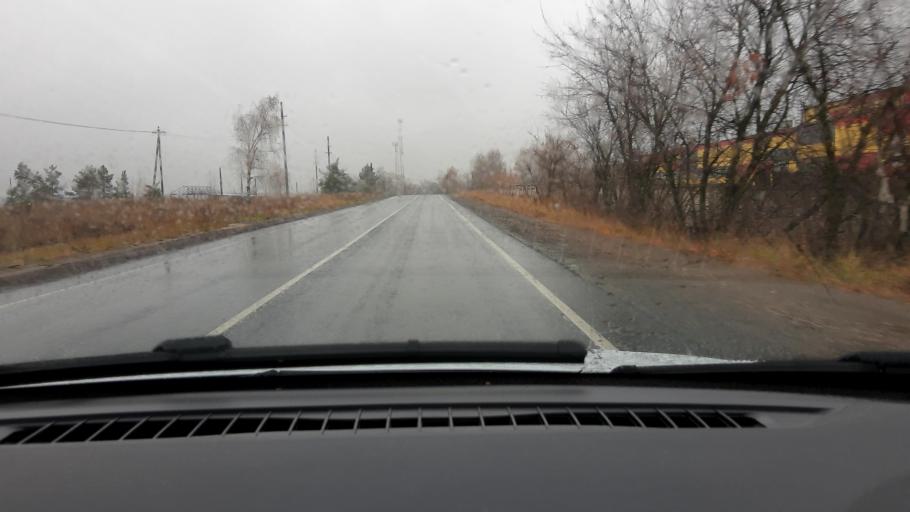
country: RU
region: Nizjnij Novgorod
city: Babino
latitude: 56.2859
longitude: 43.5996
